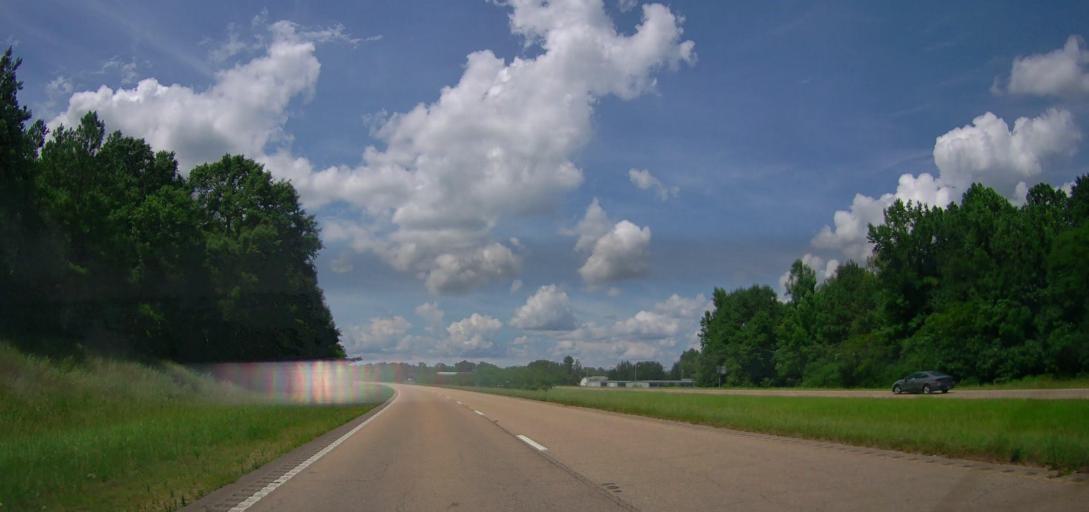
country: US
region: Mississippi
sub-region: Lee County
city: Nettleton
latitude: 34.0702
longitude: -88.6272
